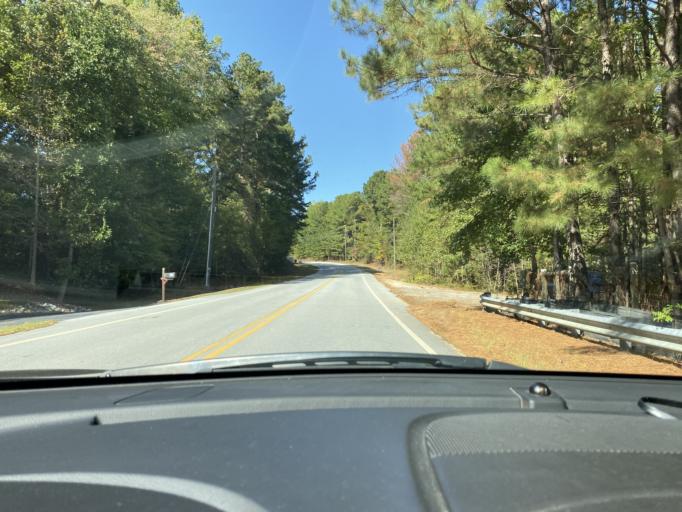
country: US
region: Georgia
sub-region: Gwinnett County
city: Grayson
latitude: 33.9024
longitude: -83.9187
